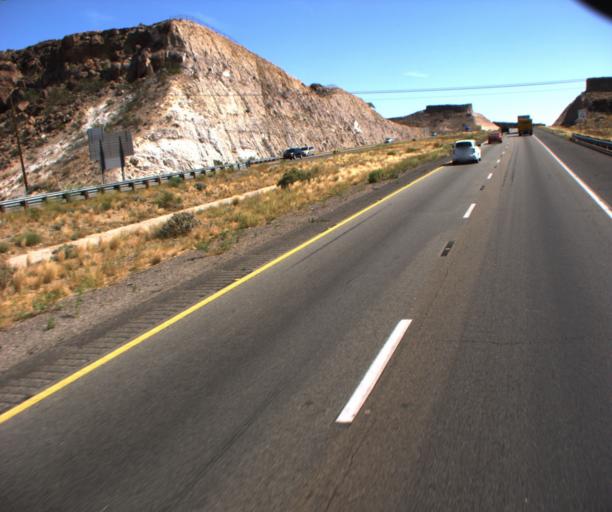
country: US
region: Arizona
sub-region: Mohave County
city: Kingman
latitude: 35.2037
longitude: -114.0631
